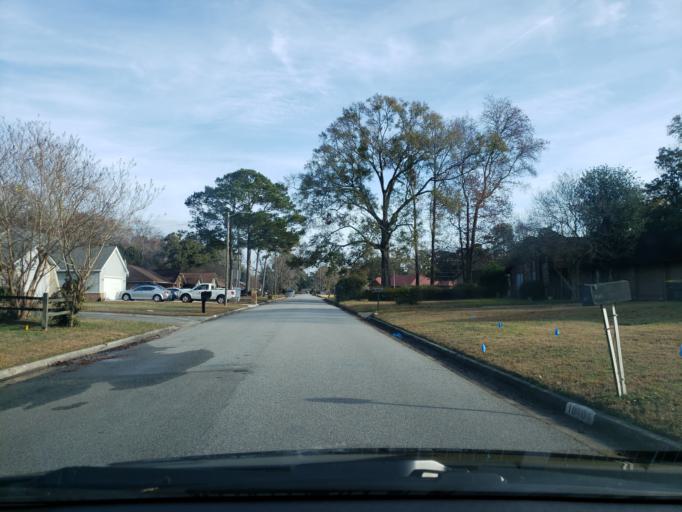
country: US
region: Georgia
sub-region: Chatham County
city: Montgomery
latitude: 31.9969
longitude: -81.1459
